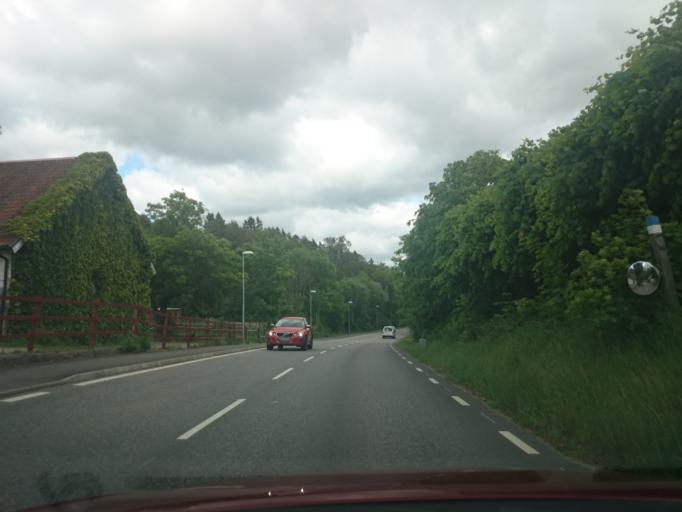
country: SE
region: Vaestra Goetaland
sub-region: Molndal
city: Moelndal
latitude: 57.6722
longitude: 12.0613
